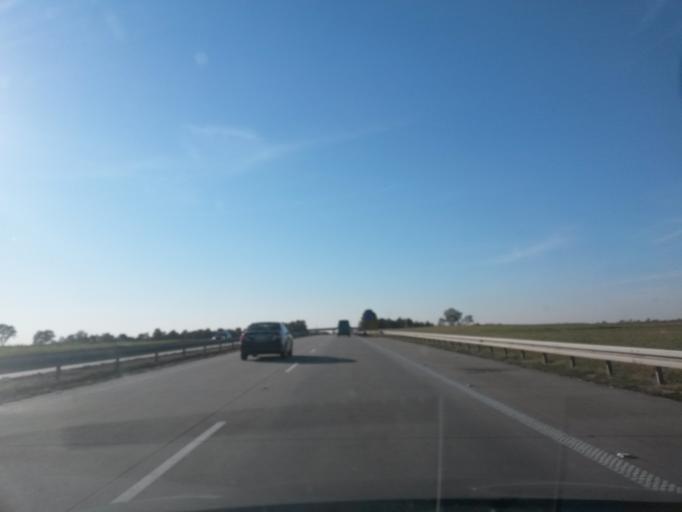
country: PL
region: Lower Silesian Voivodeship
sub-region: Powiat sredzki
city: Udanin
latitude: 51.0643
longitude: 16.4984
